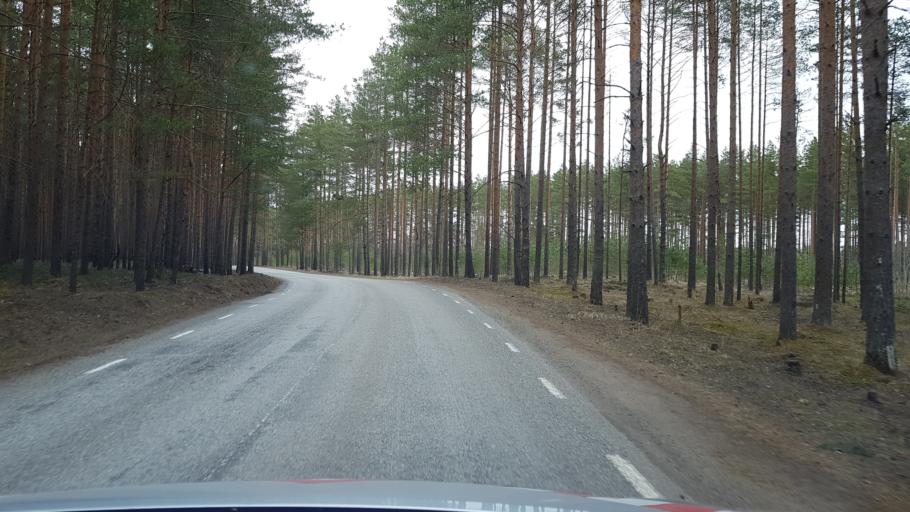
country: EE
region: Ida-Virumaa
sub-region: Narva-Joesuu linn
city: Narva-Joesuu
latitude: 59.4224
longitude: 28.1142
